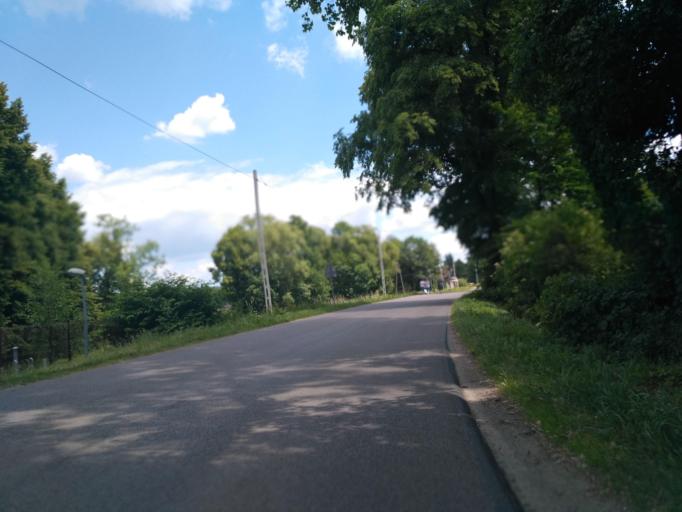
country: PL
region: Subcarpathian Voivodeship
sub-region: Powiat debicki
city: Brzostek
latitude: 49.8619
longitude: 21.4486
